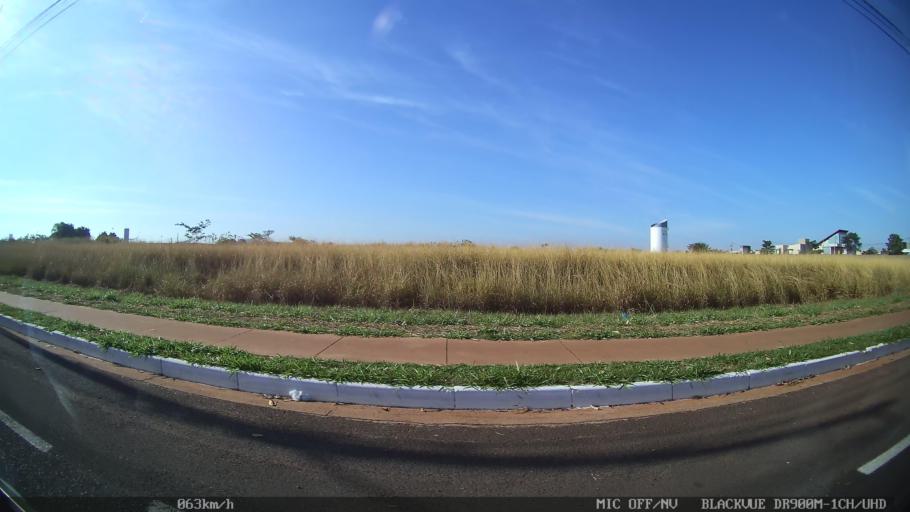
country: BR
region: Sao Paulo
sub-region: Sao Jose Do Rio Preto
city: Sao Jose do Rio Preto
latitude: -20.7740
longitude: -49.3337
